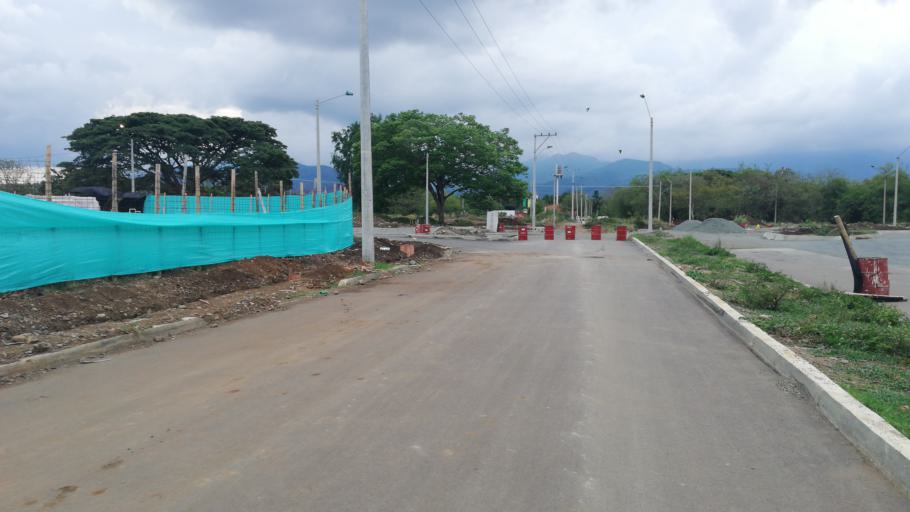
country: CO
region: Valle del Cauca
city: Jamundi
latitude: 3.3467
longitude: -76.5209
